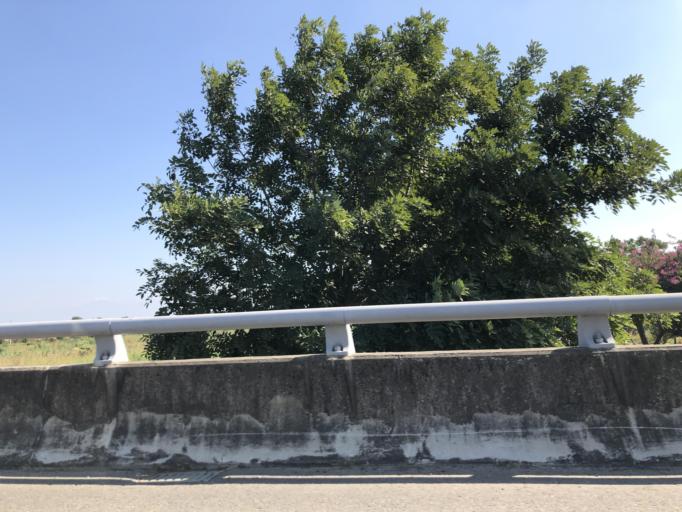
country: TW
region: Taiwan
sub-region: Tainan
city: Tainan
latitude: 23.0159
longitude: 120.2886
